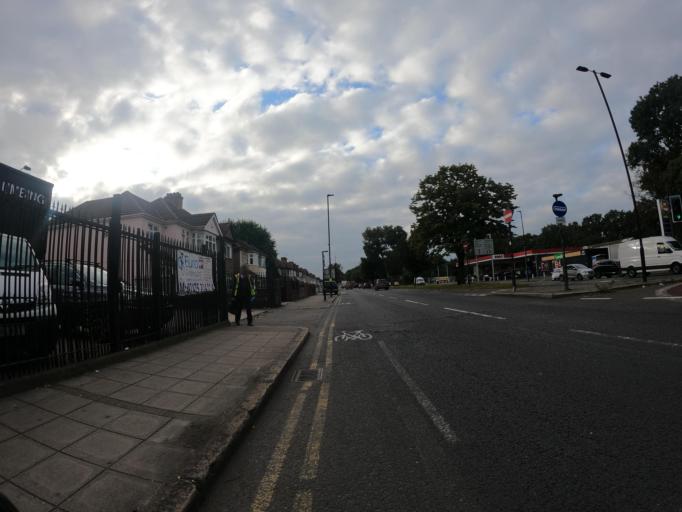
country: GB
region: England
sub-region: Greater London
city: Southall
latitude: 51.5097
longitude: -0.3583
